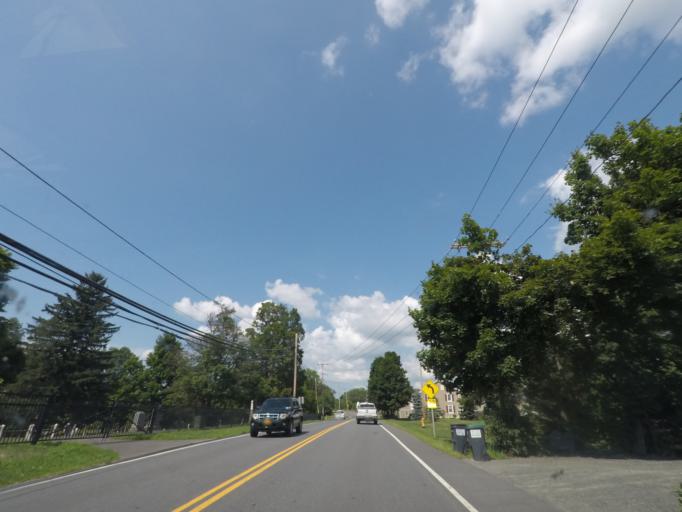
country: US
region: New York
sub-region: Albany County
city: Menands
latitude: 42.6628
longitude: -73.6883
